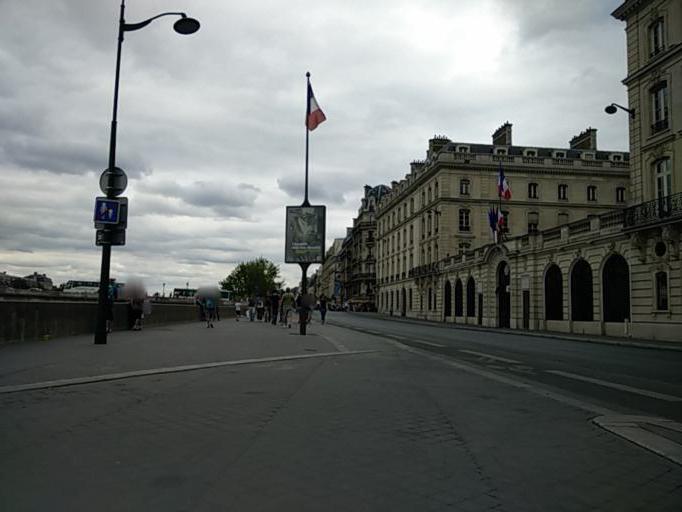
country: FR
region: Ile-de-France
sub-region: Paris
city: Paris
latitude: 48.8601
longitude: 2.3280
